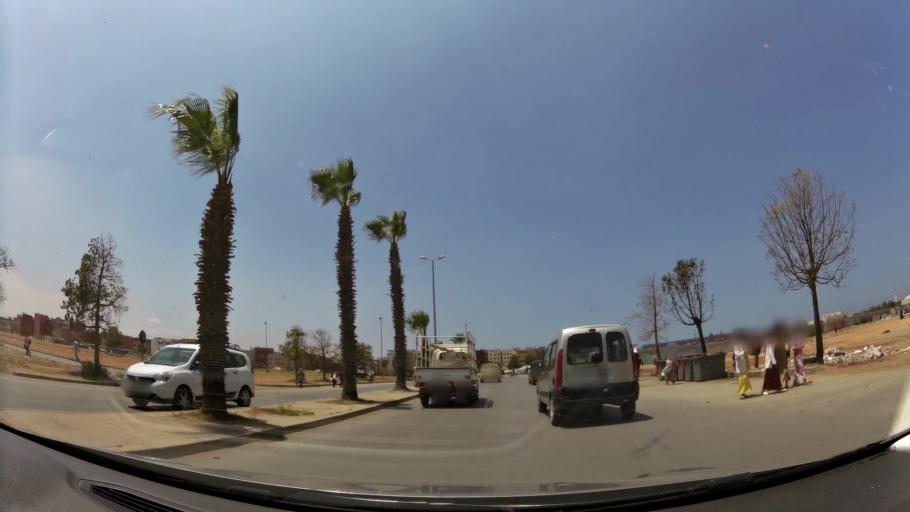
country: MA
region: Rabat-Sale-Zemmour-Zaer
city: Sale
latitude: 34.0575
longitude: -6.7910
